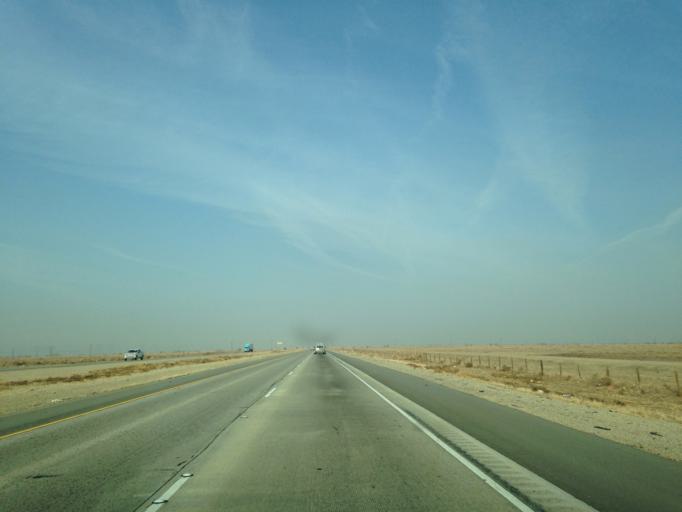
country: US
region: California
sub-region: Kern County
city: Rosedale
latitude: 35.3162
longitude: -119.2811
